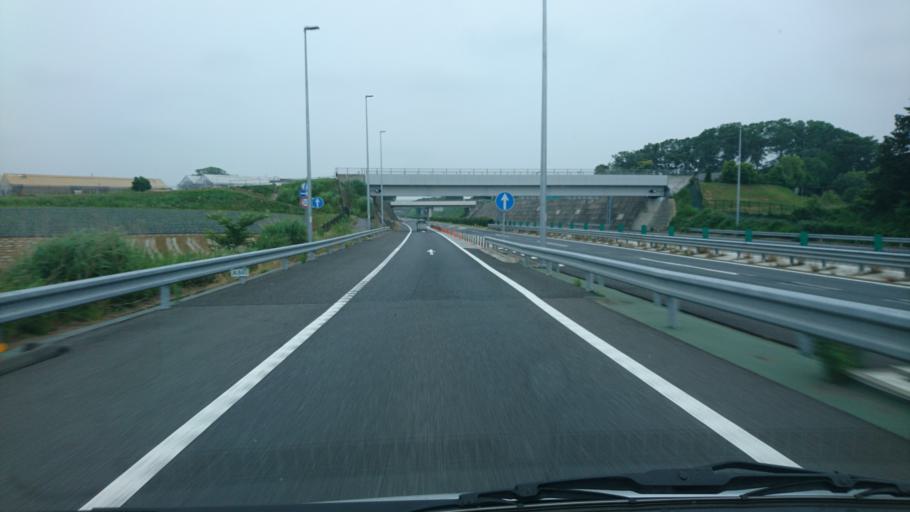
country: JP
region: Chiba
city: Narita
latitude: 35.8098
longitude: 140.3888
